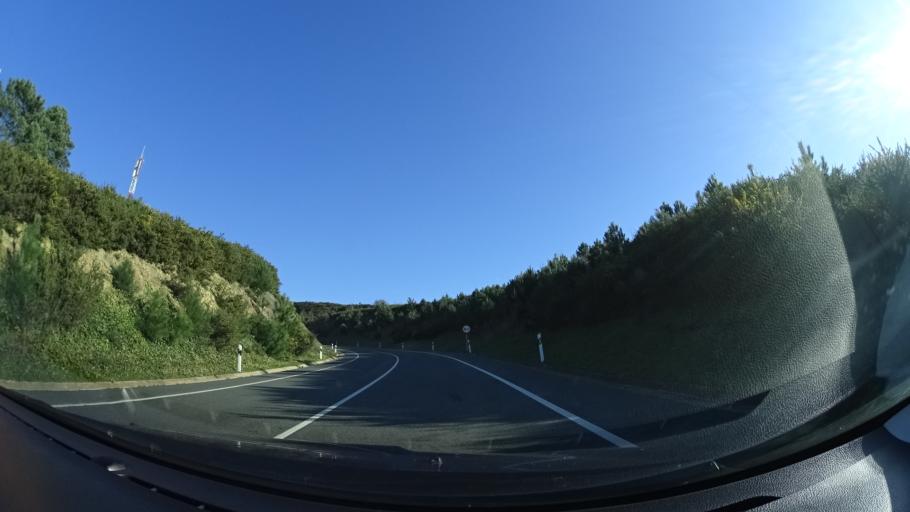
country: ES
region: Basque Country
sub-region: Bizkaia
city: Bakio
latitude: 43.4388
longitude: -2.7788
